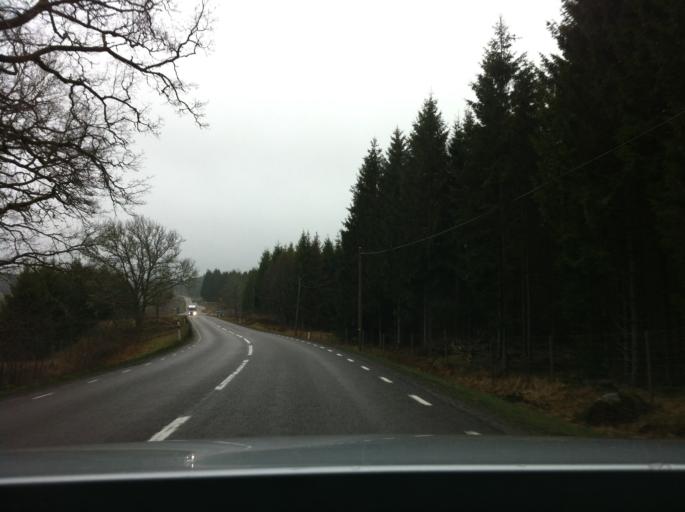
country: SE
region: Vaestra Goetaland
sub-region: Alingsas Kommun
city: Sollebrunn
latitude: 58.1739
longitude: 12.4159
